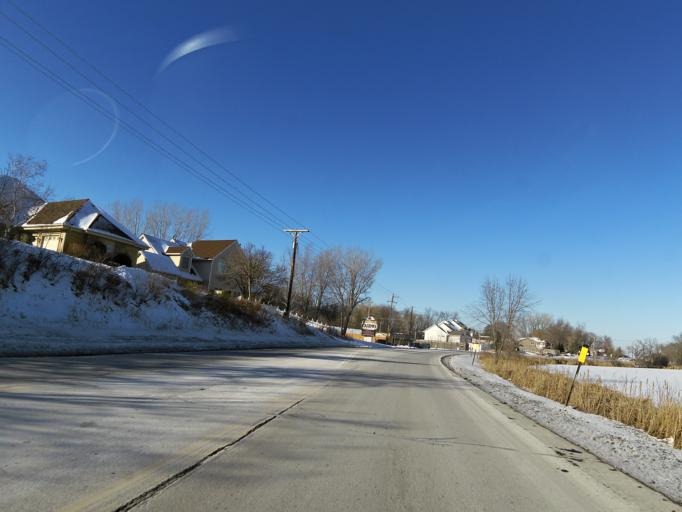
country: US
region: Minnesota
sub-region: Scott County
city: Prior Lake
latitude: 44.7360
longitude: -93.4701
